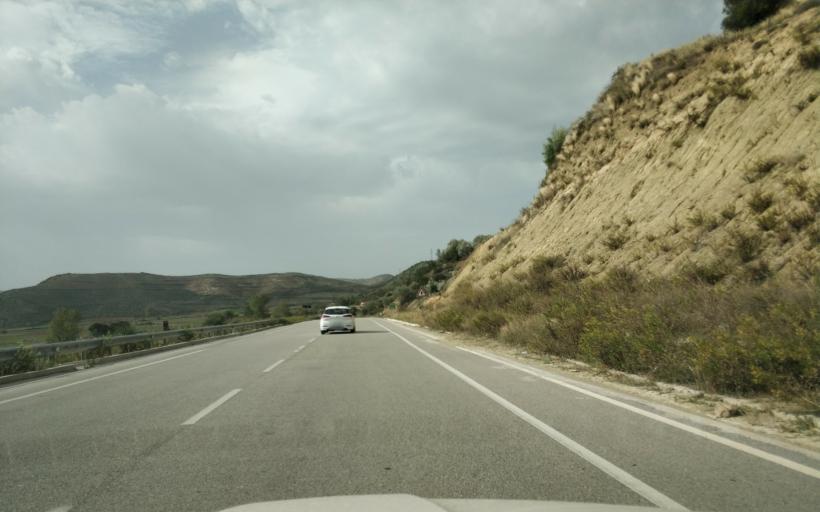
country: AL
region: Gjirokaster
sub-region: Rrethi i Tepelenes
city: Krahes
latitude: 40.3857
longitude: 19.8857
